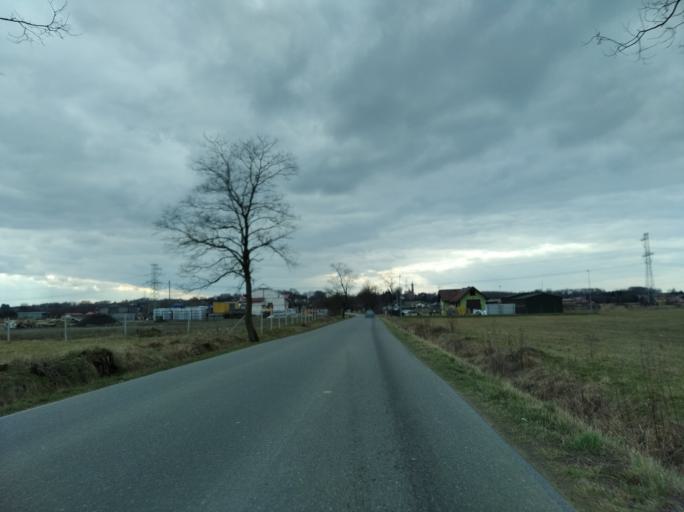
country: PL
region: Subcarpathian Voivodeship
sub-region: Powiat krosnienski
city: Odrzykon
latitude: 49.7528
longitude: 21.7110
